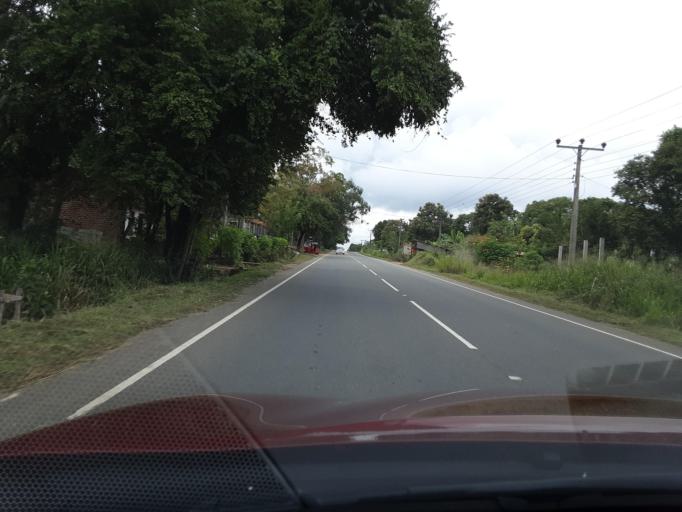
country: LK
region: Uva
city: Badulla
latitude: 7.3972
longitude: 81.1163
